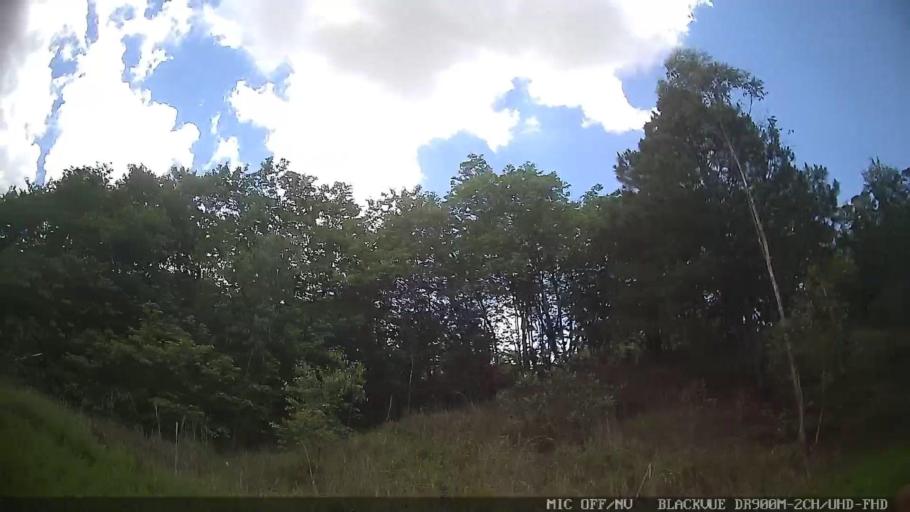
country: BR
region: Sao Paulo
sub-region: Serra Negra
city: Serra Negra
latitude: -22.6467
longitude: -46.7325
